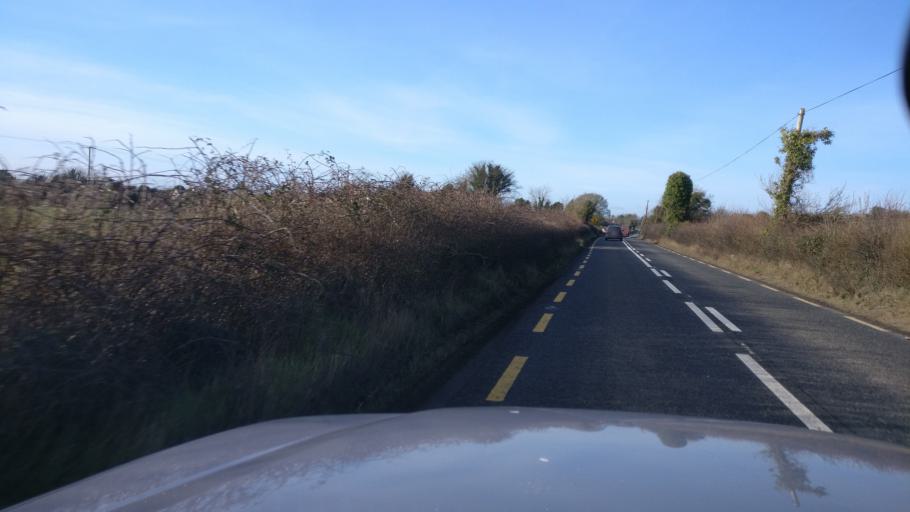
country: IE
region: Leinster
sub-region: Uibh Fhaili
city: Tullamore
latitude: 53.1929
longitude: -7.4118
